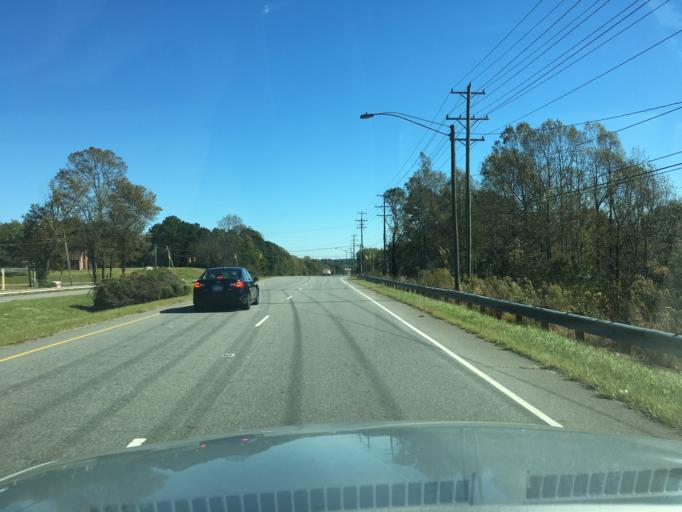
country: US
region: North Carolina
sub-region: Catawba County
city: Hickory
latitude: 35.7278
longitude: -81.3005
